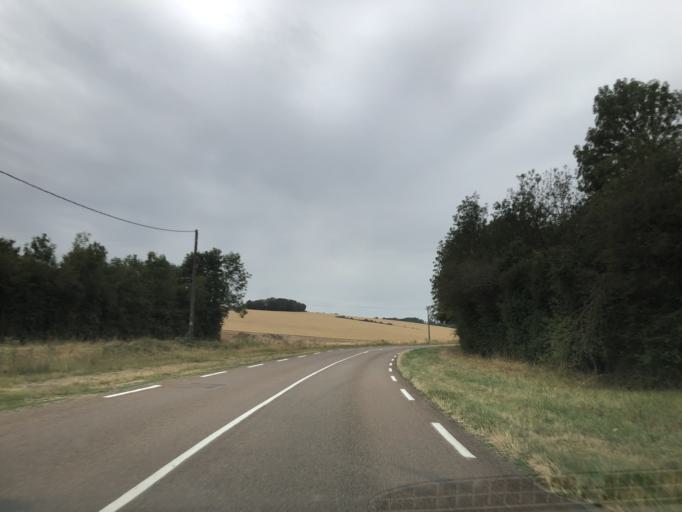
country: FR
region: Bourgogne
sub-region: Departement de l'Yonne
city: Saint-Julien-du-Sault
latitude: 47.9300
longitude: 3.2439
